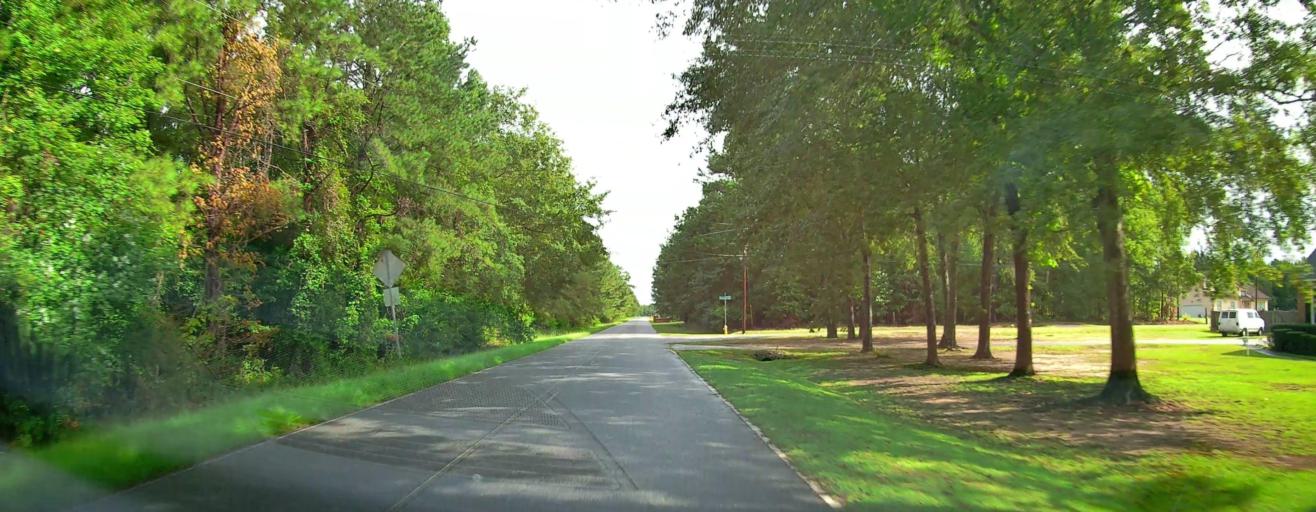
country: US
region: Georgia
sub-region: Bibb County
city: West Point
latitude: 32.7998
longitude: -83.7840
